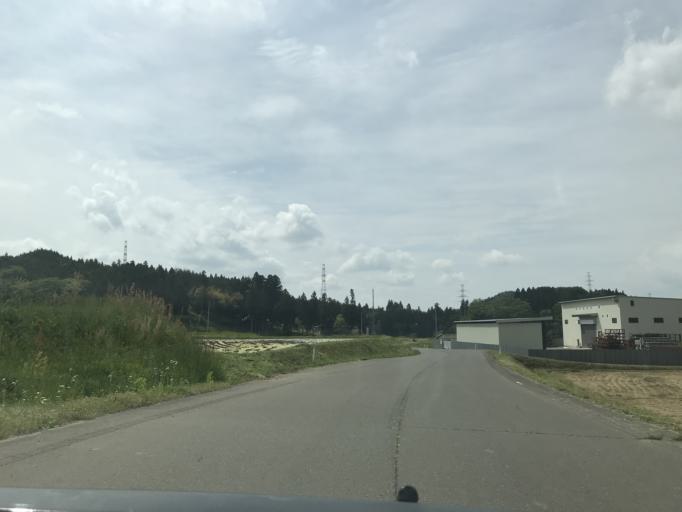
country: JP
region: Iwate
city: Ichinoseki
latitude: 38.8700
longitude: 140.9804
